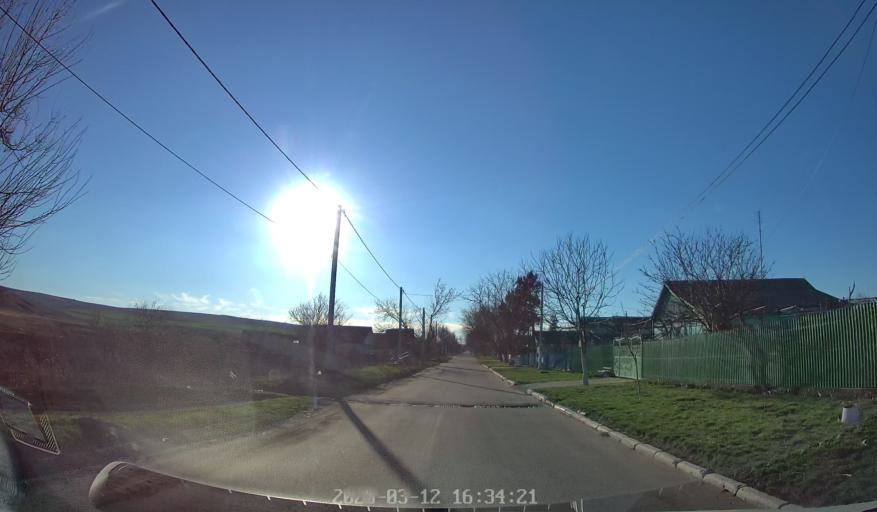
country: MD
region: Anenii Noi
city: Anenii Noi
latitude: 46.8138
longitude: 29.2082
